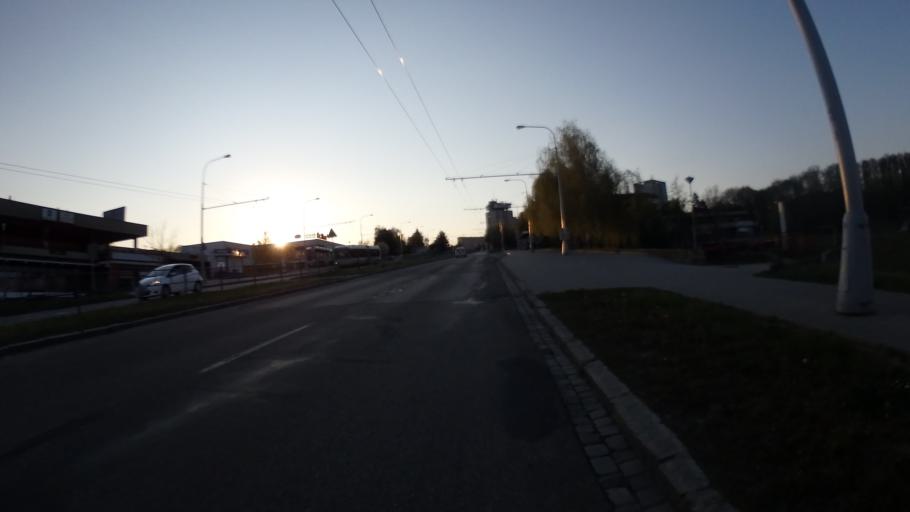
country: CZ
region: South Moravian
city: Ostopovice
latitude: 49.1946
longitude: 16.5406
